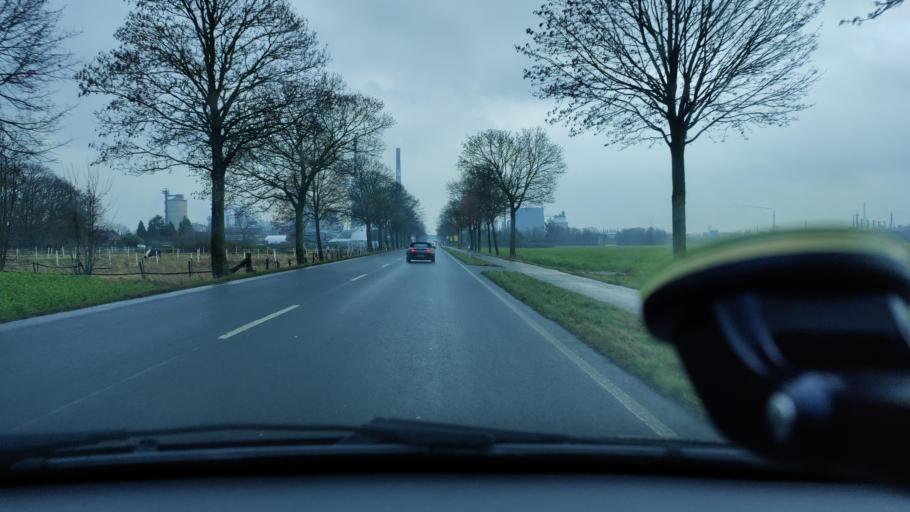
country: DE
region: North Rhine-Westphalia
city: Rheinberg
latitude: 51.5691
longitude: 6.5712
